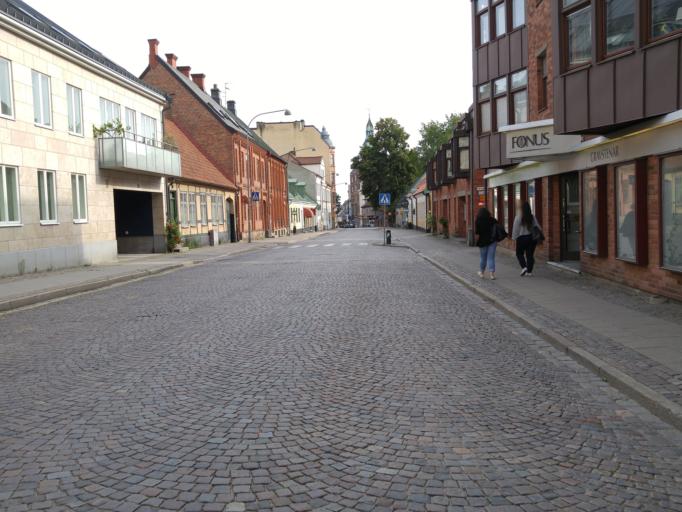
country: SE
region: Skane
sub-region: Lunds Kommun
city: Lund
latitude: 55.7077
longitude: 13.1927
